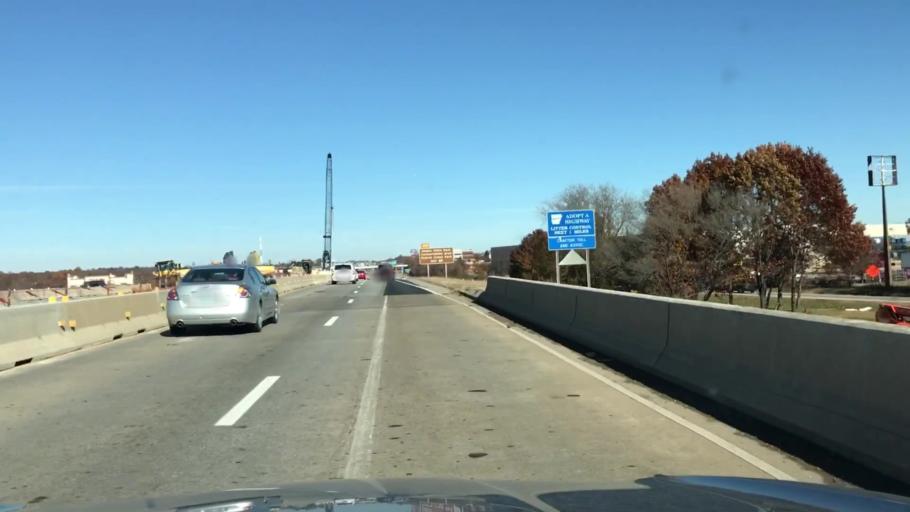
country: US
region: Arkansas
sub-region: Benton County
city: Bentonville
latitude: 36.3352
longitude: -94.1832
